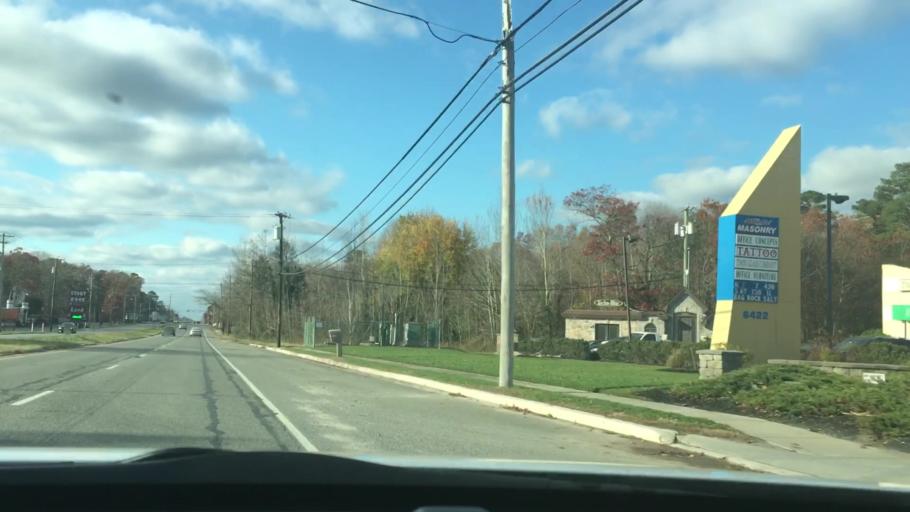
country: US
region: New Jersey
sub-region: Atlantic County
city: Pomona
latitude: 39.4224
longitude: -74.5891
